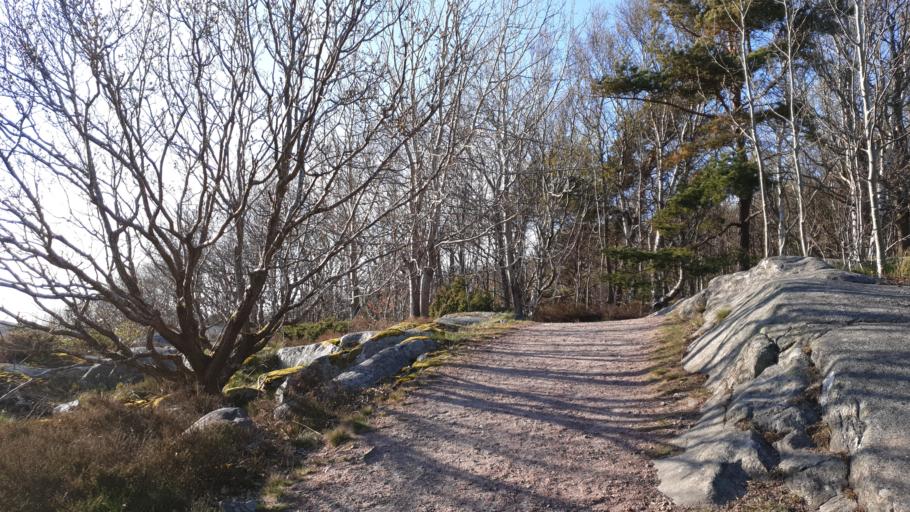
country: SE
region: Vaestra Goetaland
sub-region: Goteborg
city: Billdal
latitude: 57.5887
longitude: 11.9144
